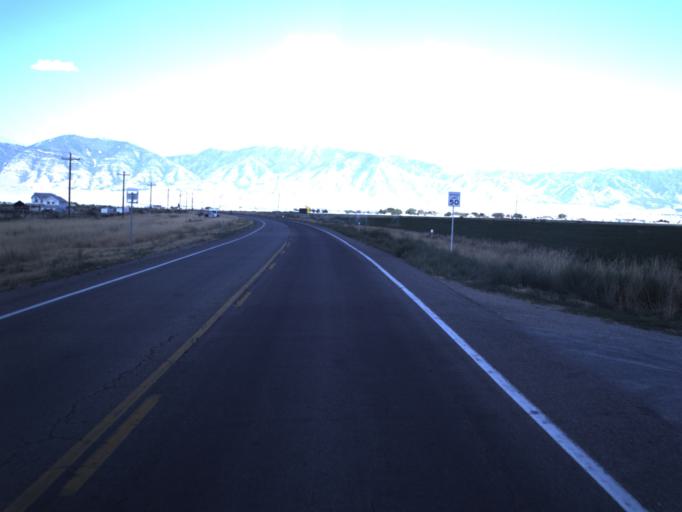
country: US
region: Utah
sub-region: Tooele County
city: Grantsville
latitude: 40.5996
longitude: -112.4138
